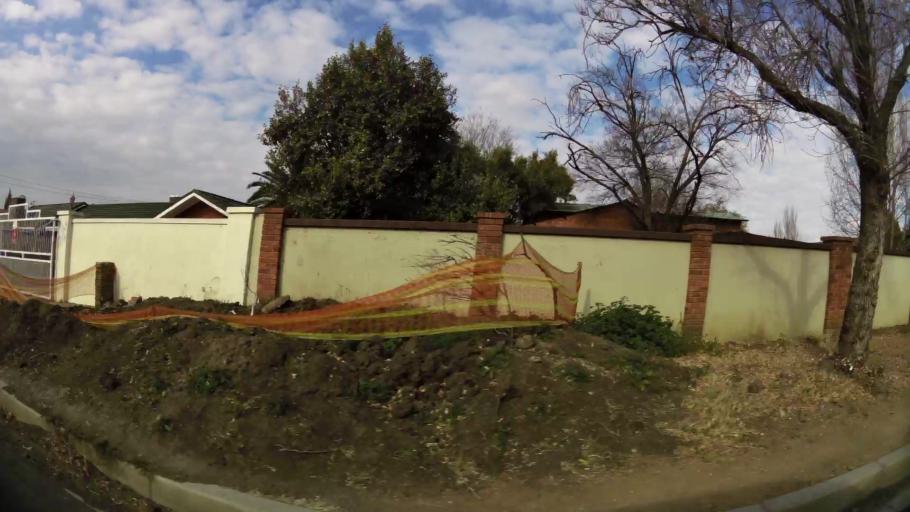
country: ZA
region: Orange Free State
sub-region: Mangaung Metropolitan Municipality
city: Bloemfontein
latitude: -29.0852
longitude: 26.2323
